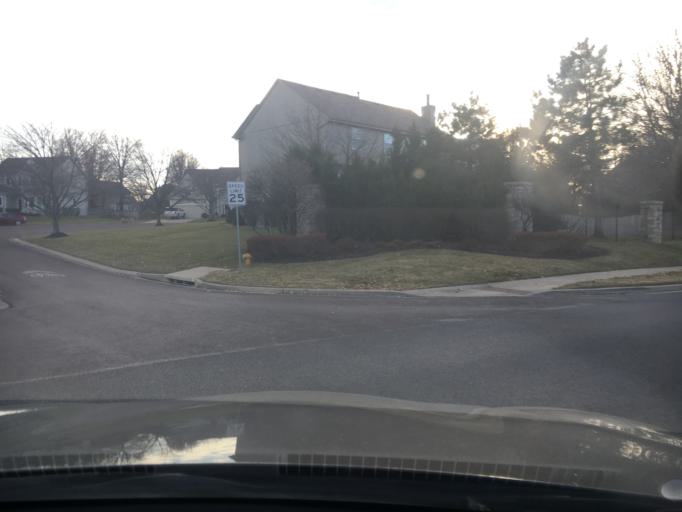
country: US
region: Kansas
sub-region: Johnson County
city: Lenexa
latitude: 38.8692
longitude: -94.6818
